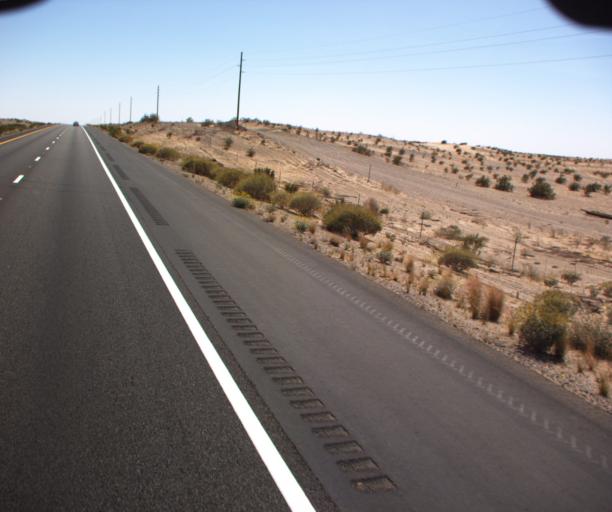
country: US
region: Arizona
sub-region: Yuma County
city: Somerton
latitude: 32.5429
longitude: -114.5623
